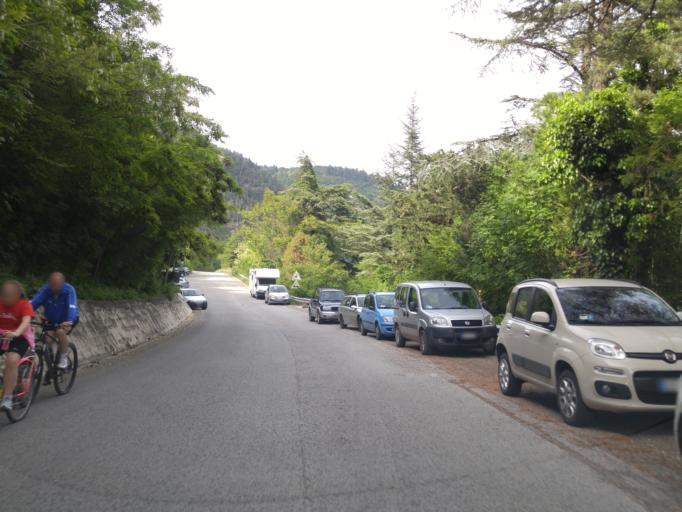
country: IT
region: The Marches
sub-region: Provincia di Pesaro e Urbino
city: Canavaccio
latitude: 43.6571
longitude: 12.7341
